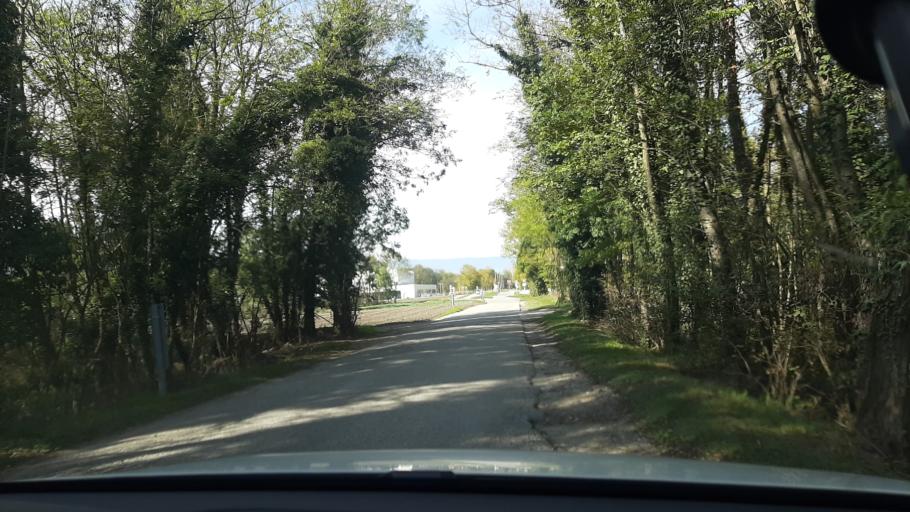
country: FR
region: Rhone-Alpes
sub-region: Departement de la Savoie
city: Montmelian
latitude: 45.4728
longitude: 6.0364
